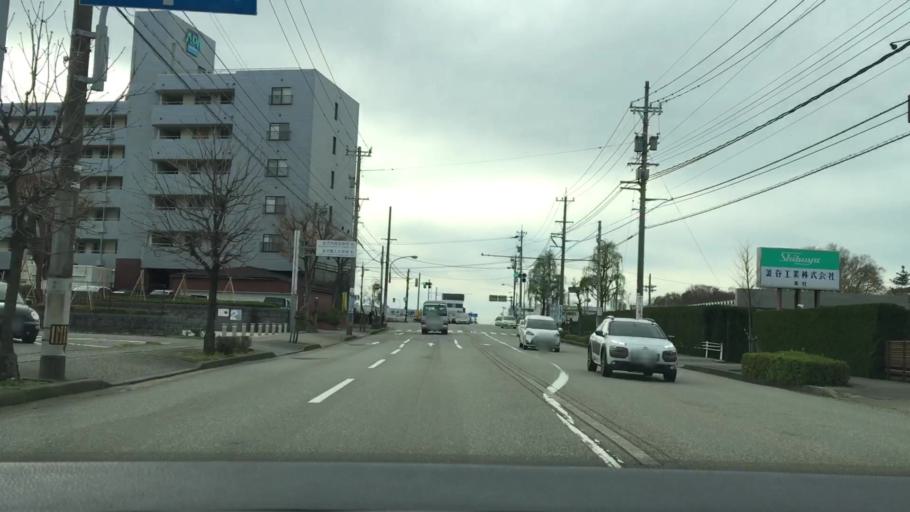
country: JP
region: Ishikawa
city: Kanazawa-shi
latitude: 36.5706
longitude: 136.6369
